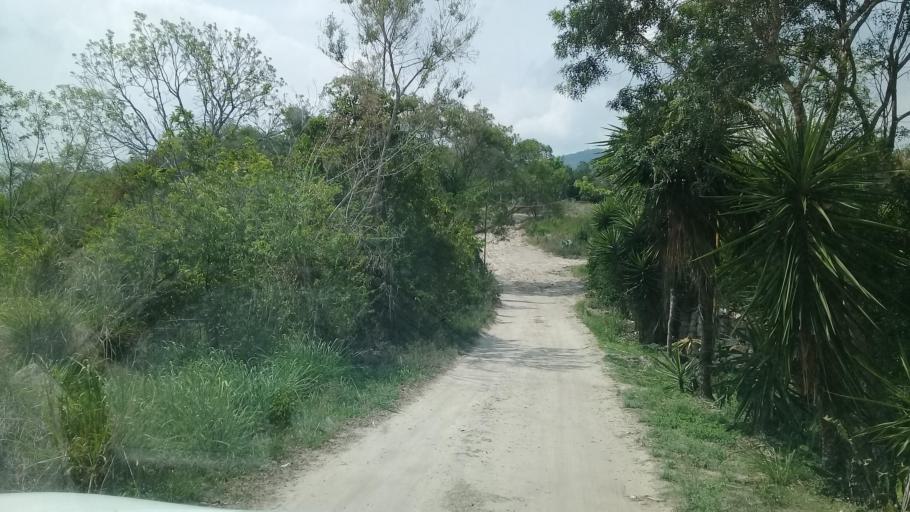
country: MX
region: Veracruz
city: Jalcomulco
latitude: 19.3866
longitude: -96.7913
